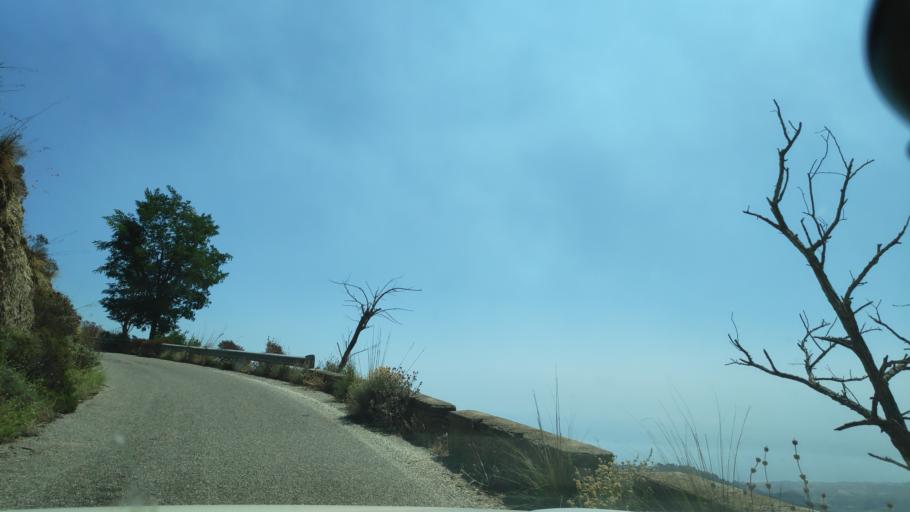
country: IT
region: Calabria
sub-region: Provincia di Reggio Calabria
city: Bova
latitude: 38.0016
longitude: 15.9279
